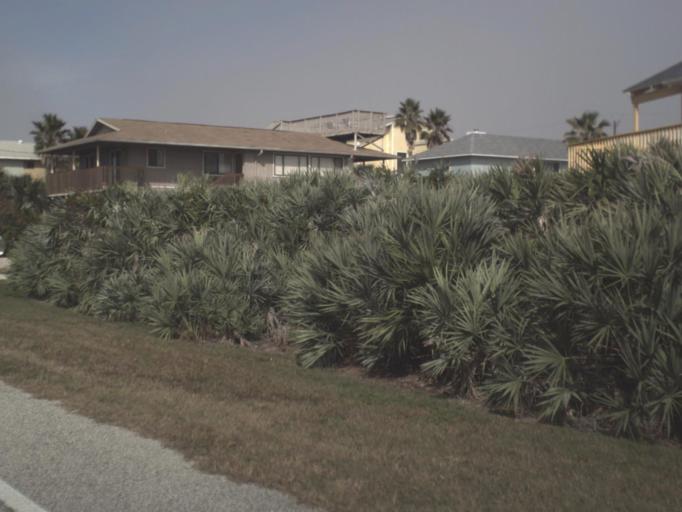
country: US
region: Florida
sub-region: Volusia County
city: Edgewater
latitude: 28.9607
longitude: -80.8470
